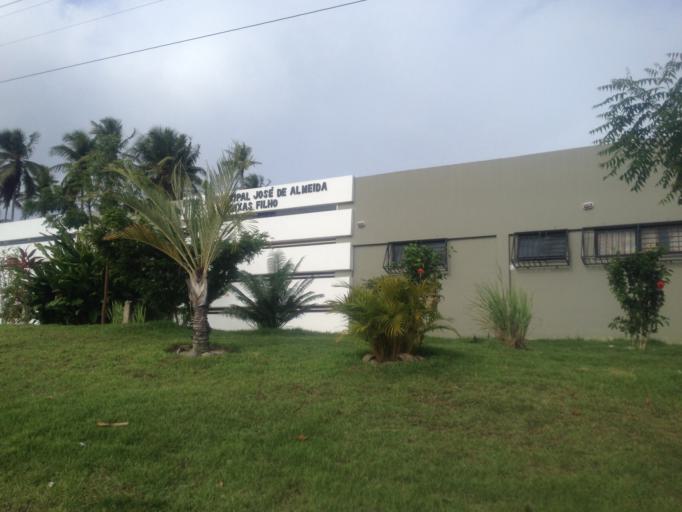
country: BR
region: Bahia
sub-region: Mata De Sao Joao
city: Mata de Sao Joao
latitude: -12.4937
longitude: -37.9696
